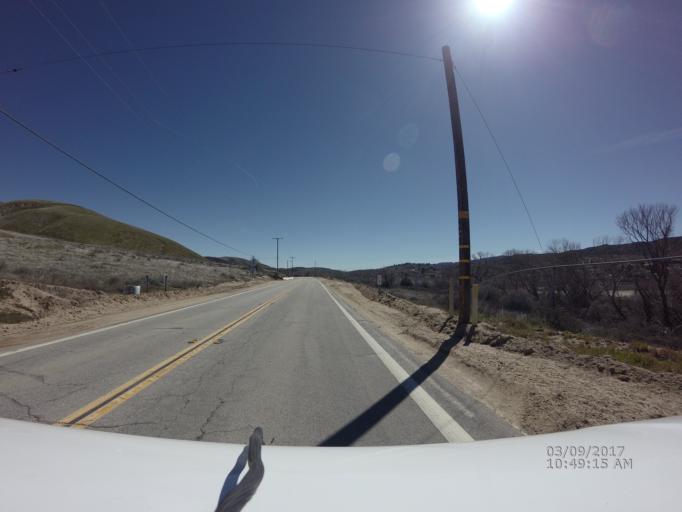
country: US
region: California
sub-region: Los Angeles County
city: Green Valley
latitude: 34.6680
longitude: -118.4029
